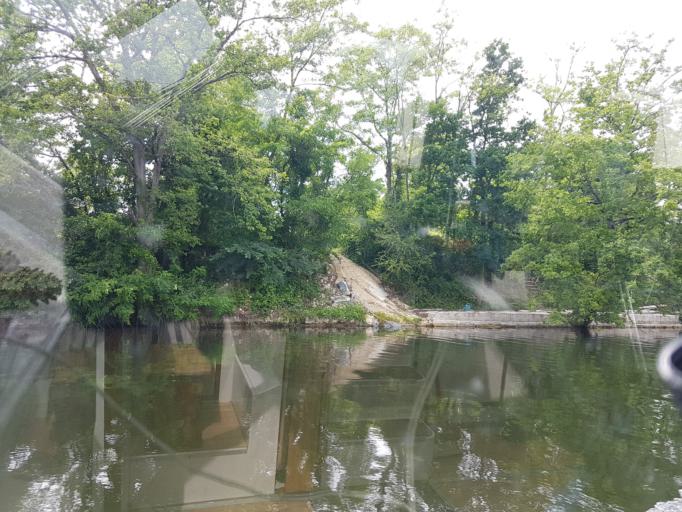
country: FR
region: Bourgogne
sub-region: Departement de l'Yonne
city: Gurgy
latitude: 47.8547
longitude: 3.5573
